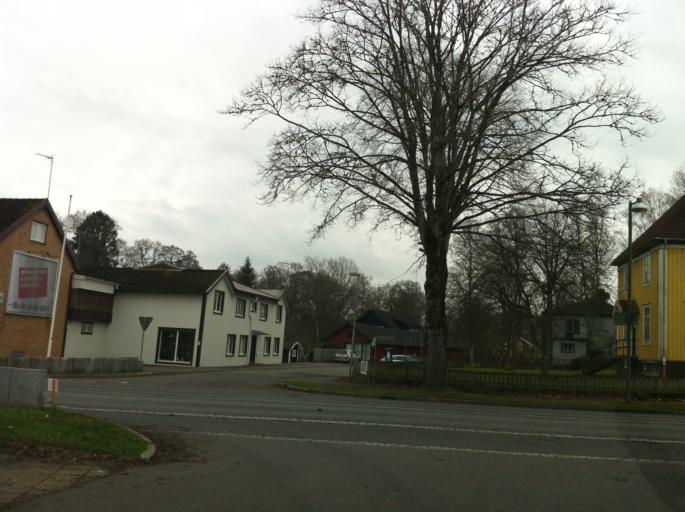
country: SE
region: Joenkoeping
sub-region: Savsjo Kommun
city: Vrigstad
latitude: 57.3566
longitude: 14.4797
